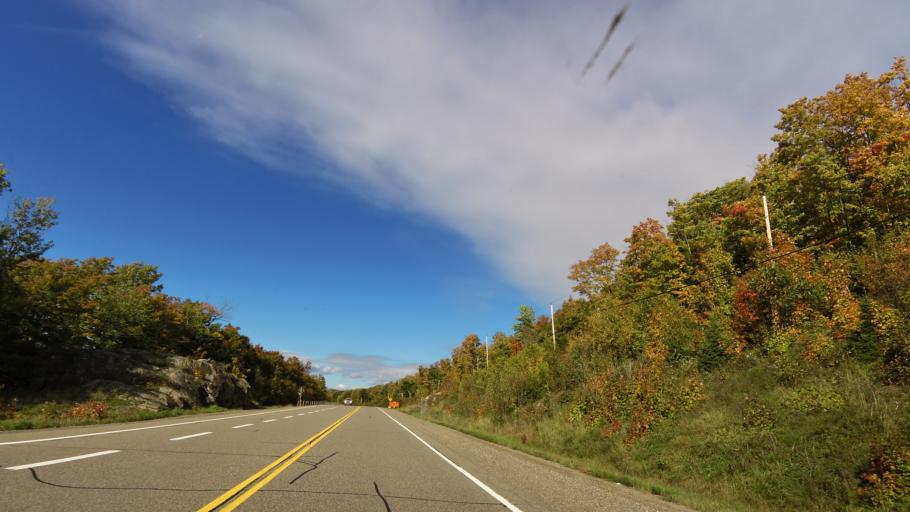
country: CA
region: Ontario
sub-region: Algoma
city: Sault Ste. Marie
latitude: 46.9376
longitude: -84.4673
